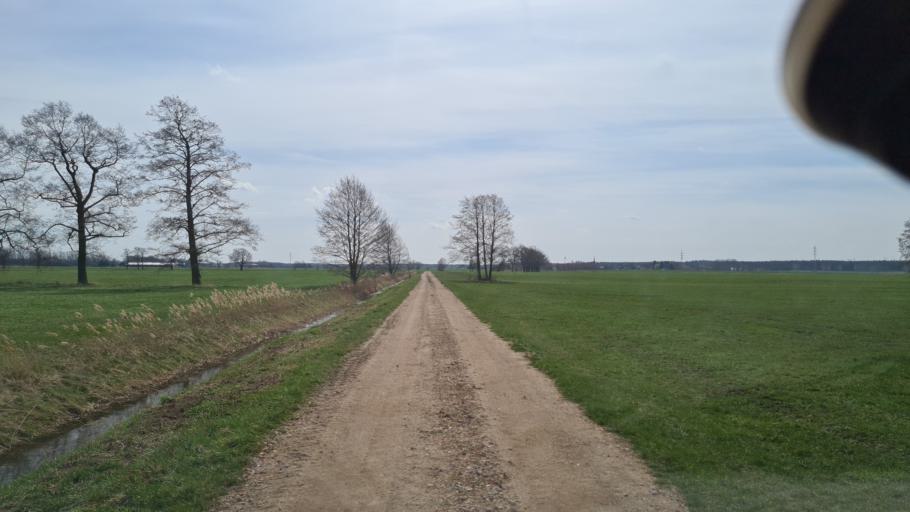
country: DE
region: Brandenburg
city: Bronkow
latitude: 51.6073
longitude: 13.9271
